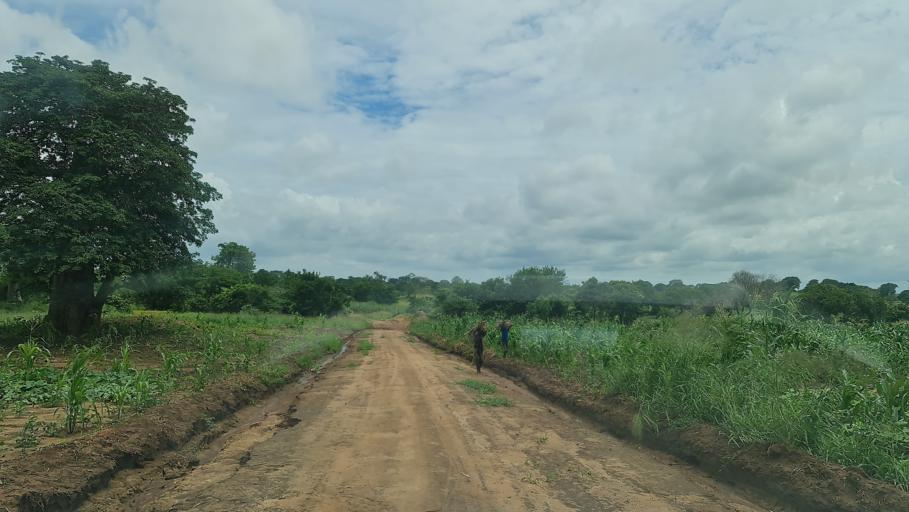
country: MZ
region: Cabo Delgado
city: Pemba
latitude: -13.5207
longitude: 40.0180
